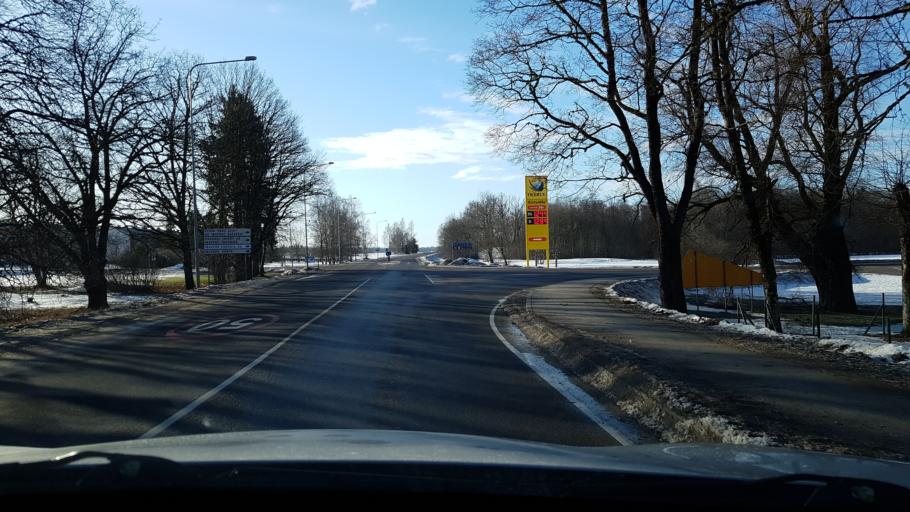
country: EE
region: Jogevamaa
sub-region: Poltsamaa linn
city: Poltsamaa
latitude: 58.7330
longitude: 25.7669
